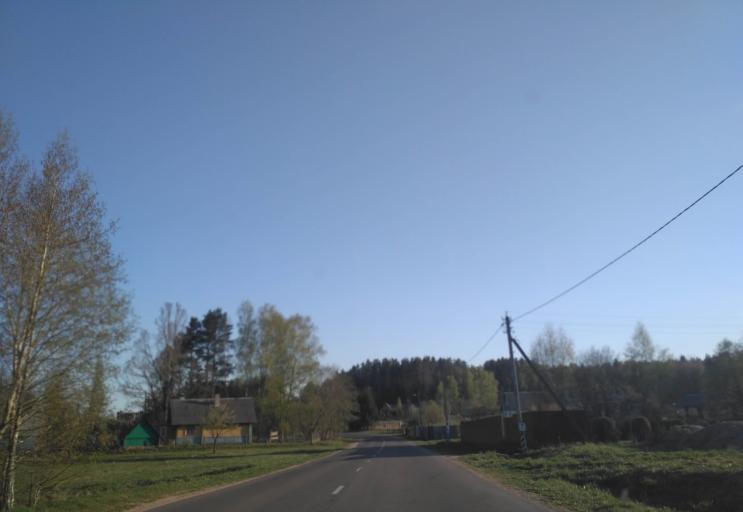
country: BY
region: Minsk
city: Radashkovichy
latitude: 54.1305
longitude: 27.2011
